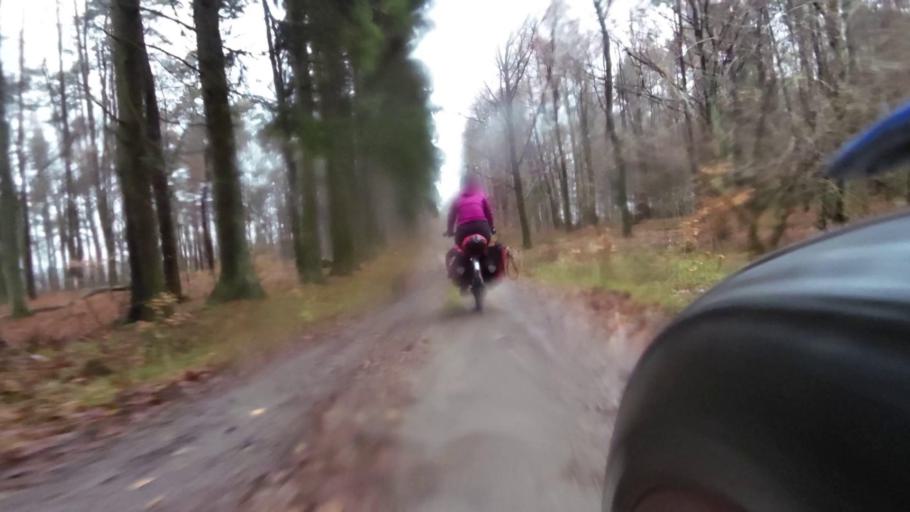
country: PL
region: West Pomeranian Voivodeship
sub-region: Powiat drawski
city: Czaplinek
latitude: 53.5158
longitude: 16.2022
